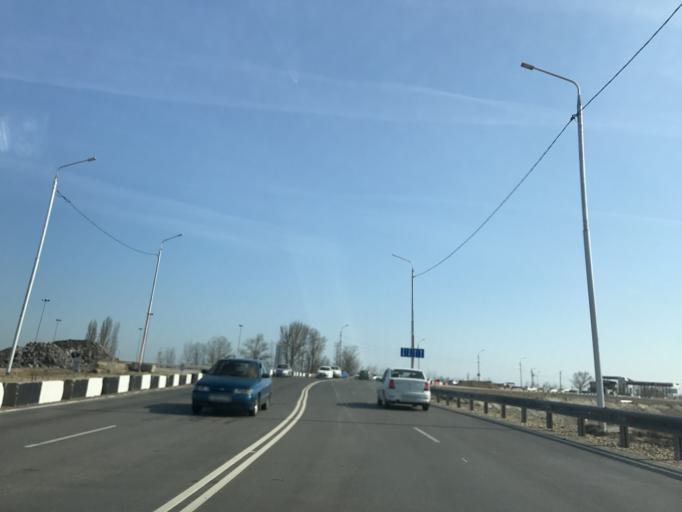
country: RU
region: Rostov
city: Rostov-na-Donu
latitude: 47.1986
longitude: 39.7291
